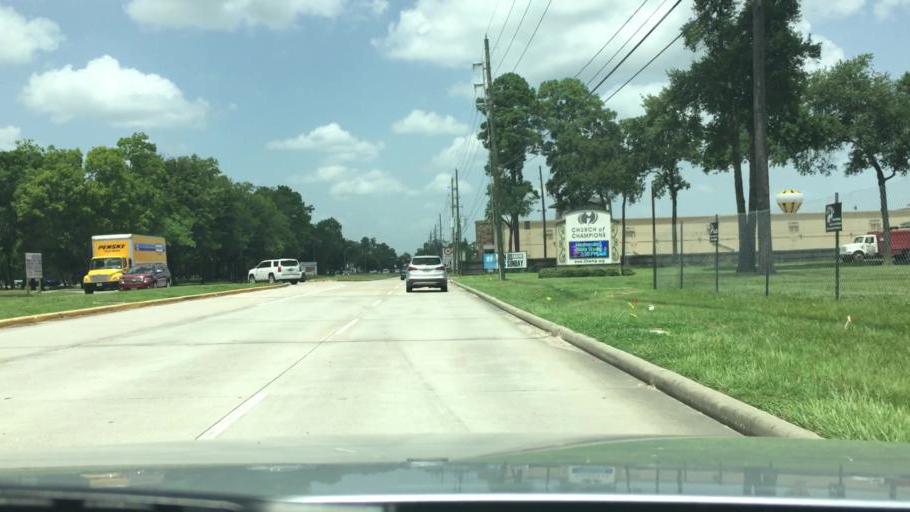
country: US
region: Texas
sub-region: Harris County
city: Hudson
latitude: 29.9654
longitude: -95.5313
